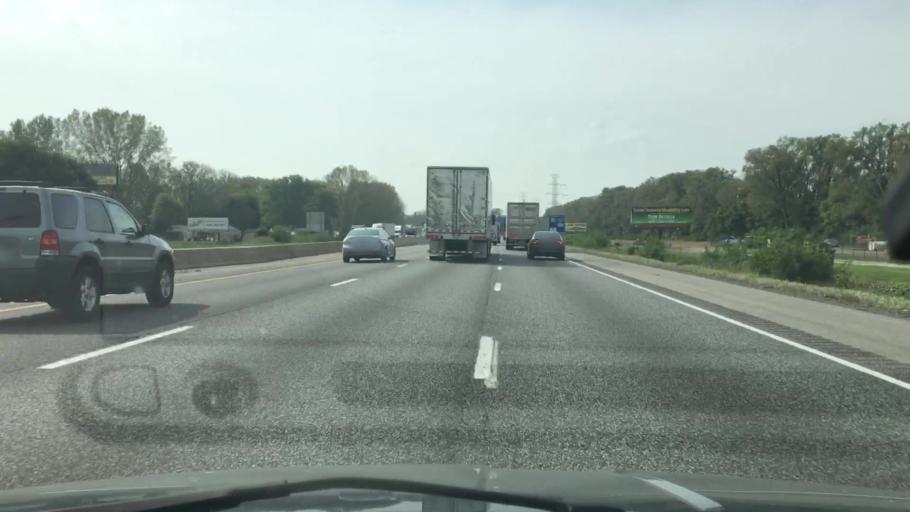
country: US
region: Indiana
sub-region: Porter County
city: Ogden Dunes
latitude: 41.5981
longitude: -87.2055
